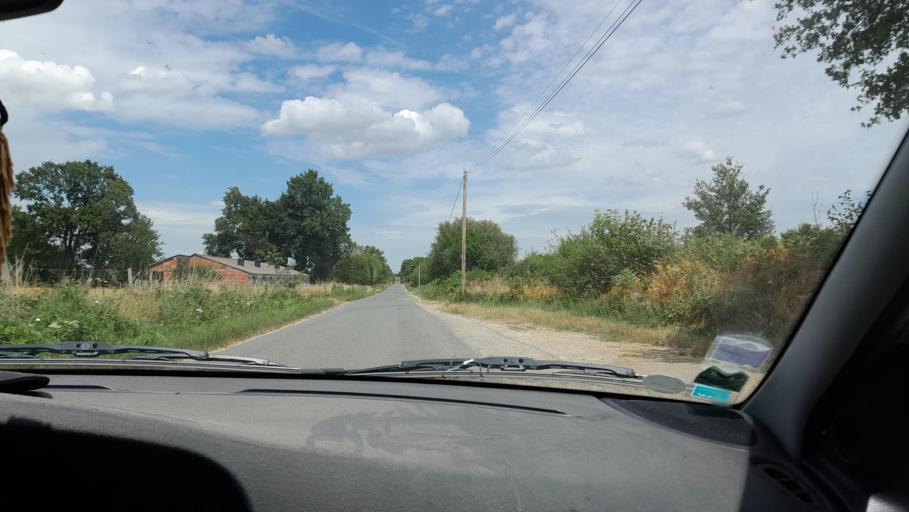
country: FR
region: Pays de la Loire
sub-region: Departement de la Mayenne
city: Saint-Pierre-la-Cour
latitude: 48.1491
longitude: -1.0327
